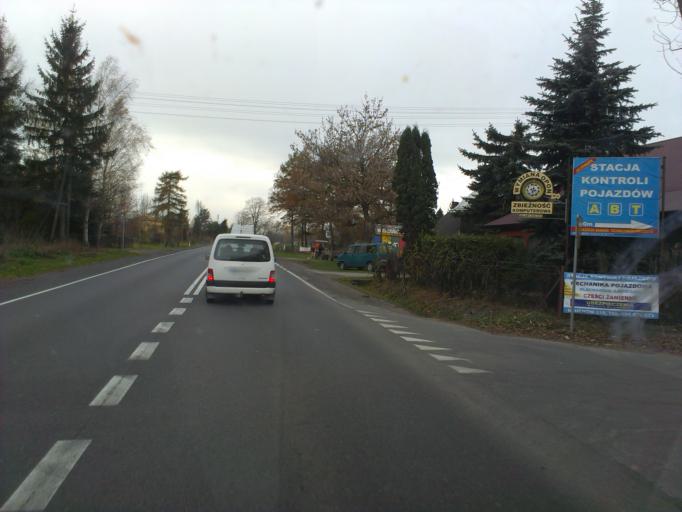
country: PL
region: Subcarpathian Voivodeship
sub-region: Powiat lancucki
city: Gluchow
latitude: 50.0806
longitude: 22.2676
